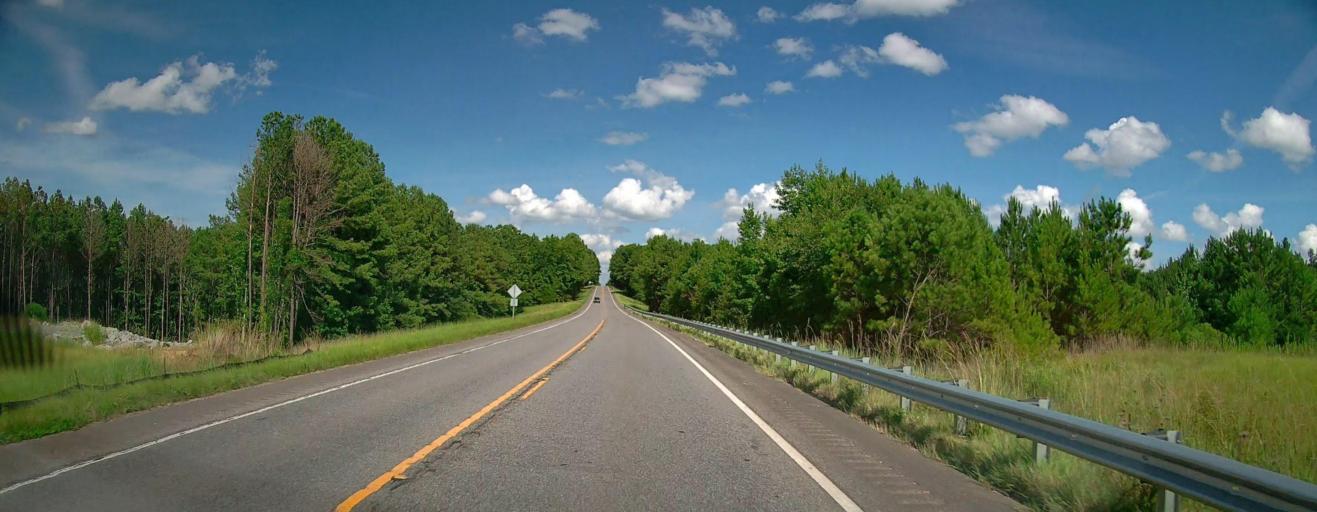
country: US
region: Alabama
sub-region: Pickens County
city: Gordo
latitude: 33.2848
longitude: -87.8514
